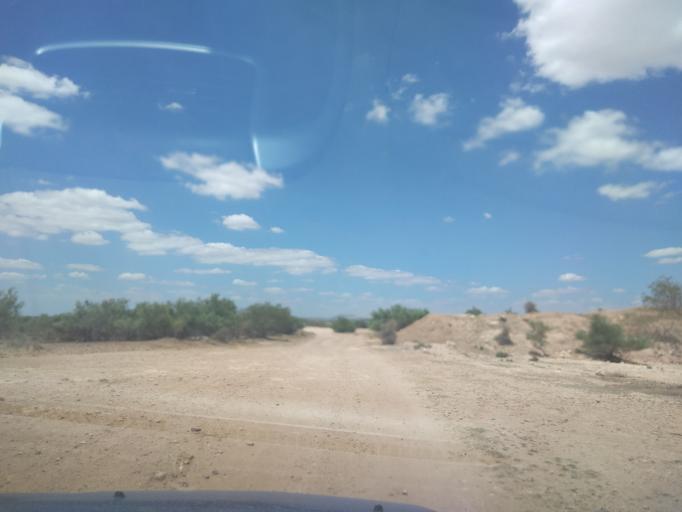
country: TN
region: Susah
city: Harqalah
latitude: 36.1655
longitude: 10.4455
